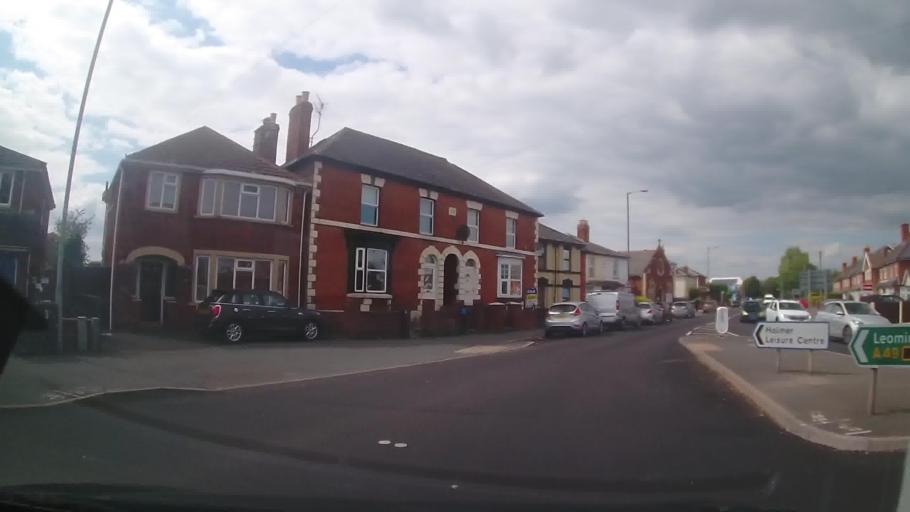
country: GB
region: England
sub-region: Herefordshire
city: Hereford
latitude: 52.0653
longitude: -2.7220
